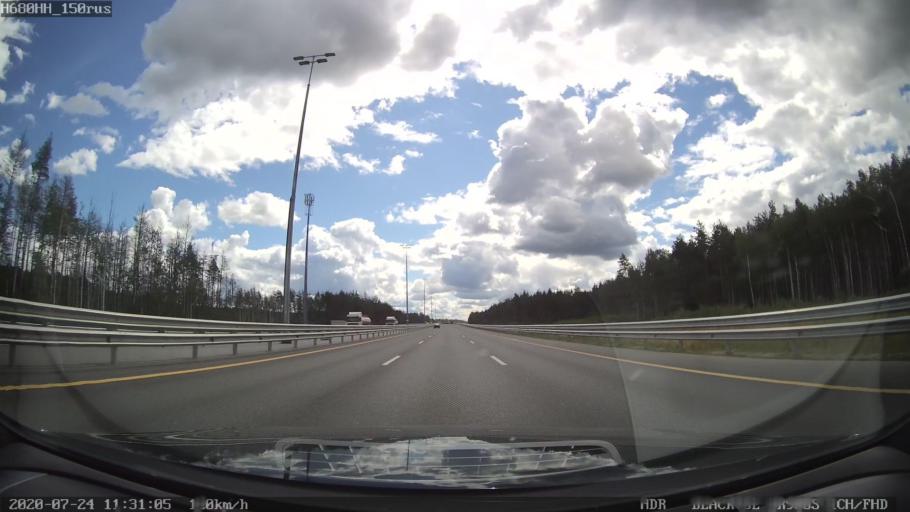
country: RU
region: Leningrad
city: Krasnyy Bor
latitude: 59.6624
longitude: 30.6269
